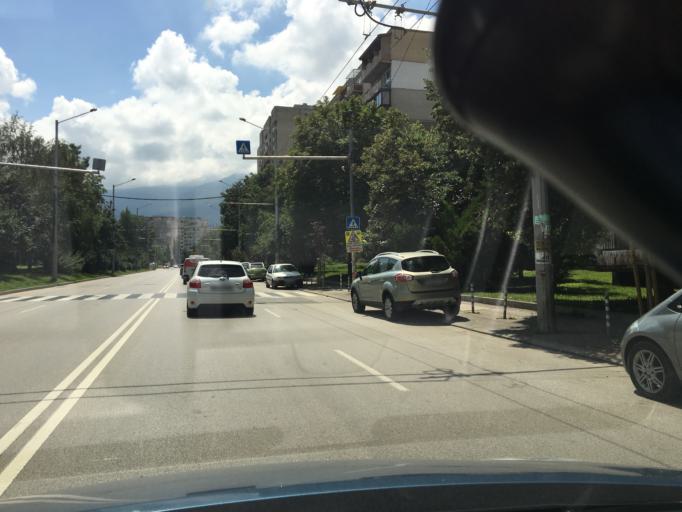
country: BG
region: Sofia-Capital
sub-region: Stolichna Obshtina
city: Sofia
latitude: 42.6678
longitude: 23.3034
